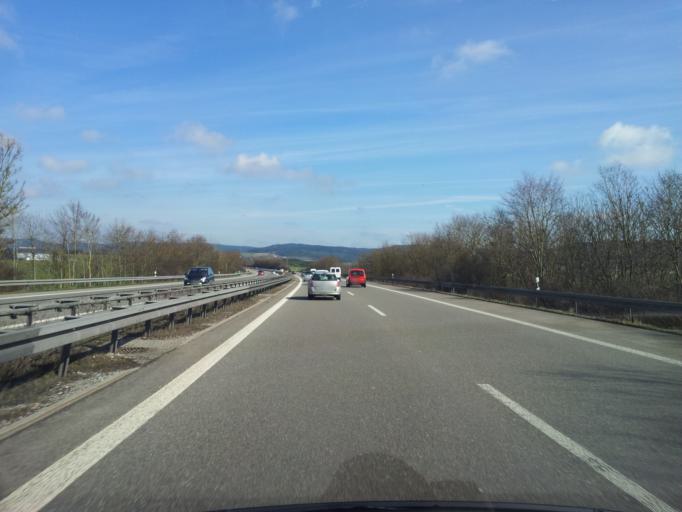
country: DE
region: Baden-Wuerttemberg
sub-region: Freiburg Region
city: Dietingen
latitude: 48.2257
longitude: 8.6491
